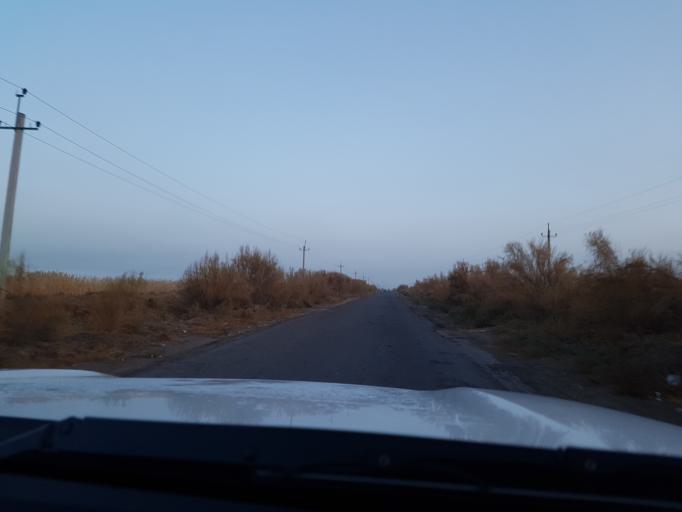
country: TM
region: Dasoguz
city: Koeneuergench
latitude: 41.7848
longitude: 58.6973
